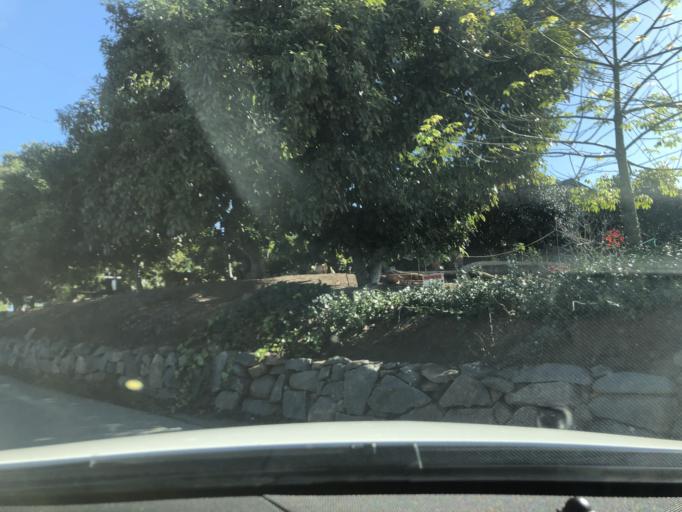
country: US
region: California
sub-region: San Diego County
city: El Cajon
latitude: 32.7838
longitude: -116.9428
